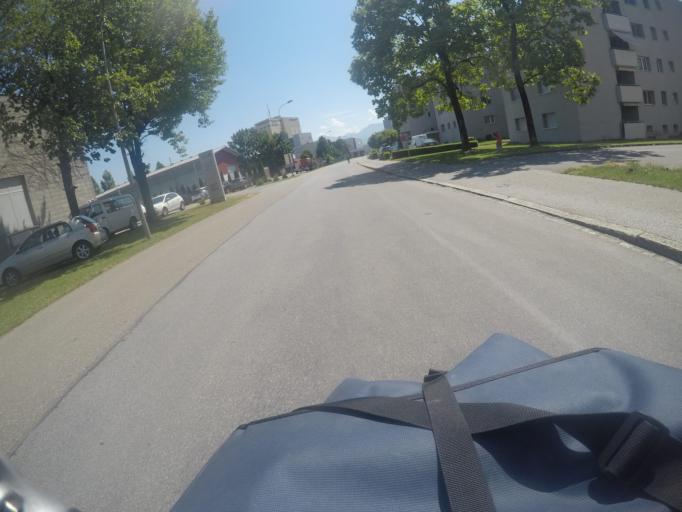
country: CH
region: Saint Gallen
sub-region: Wahlkreis Rheintal
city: Sankt Margrethen
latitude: 47.4496
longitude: 9.6470
